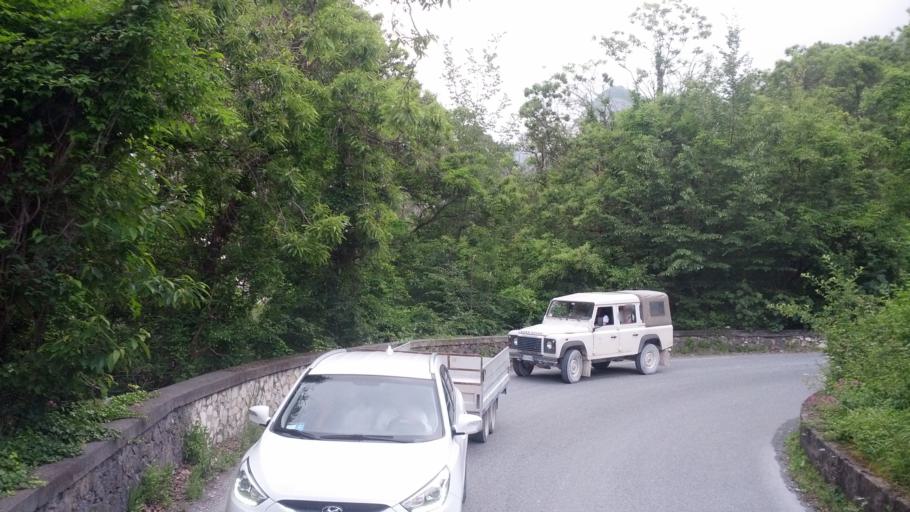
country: IT
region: Tuscany
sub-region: Provincia di Massa-Carrara
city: Massa
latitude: 44.0789
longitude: 10.1289
